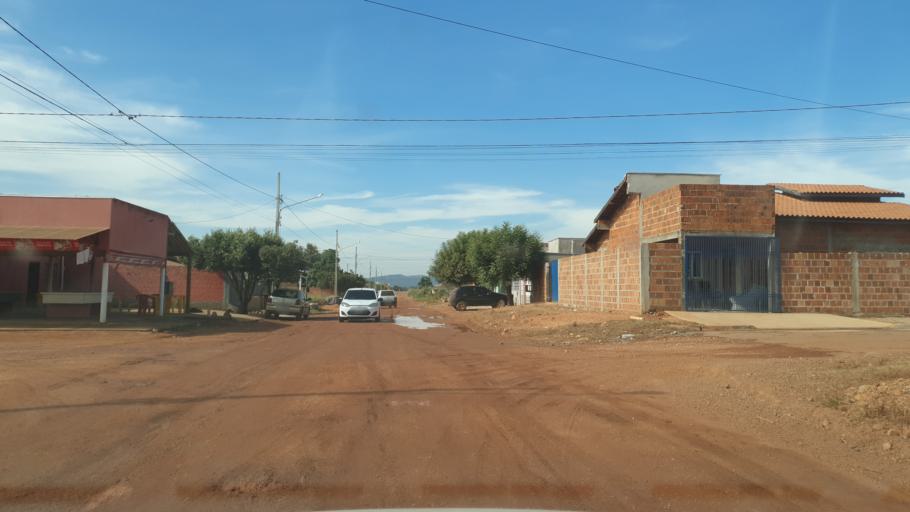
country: BR
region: Mato Grosso
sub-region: Pontes E Lacerda
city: Pontes e Lacerda
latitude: -15.2513
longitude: -59.3167
